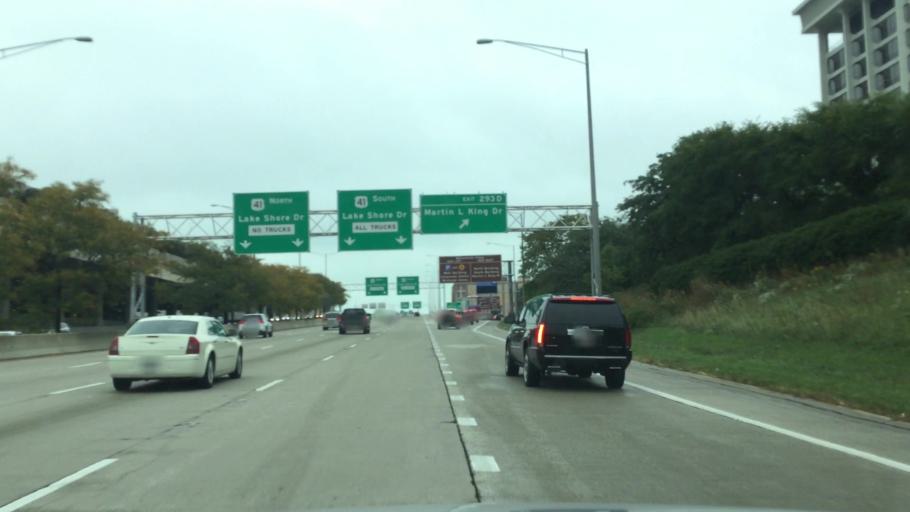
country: US
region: Illinois
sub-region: Cook County
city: Chicago
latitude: 41.8479
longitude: -87.6228
